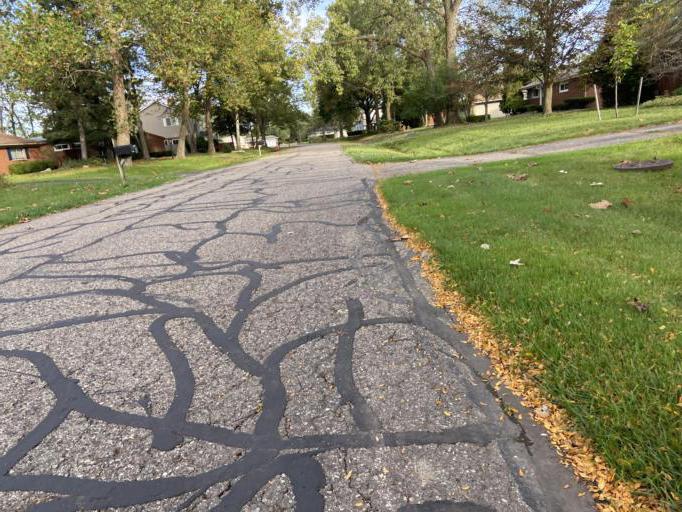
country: US
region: Michigan
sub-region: Oakland County
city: Farmington Hills
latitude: 42.5118
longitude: -83.3636
